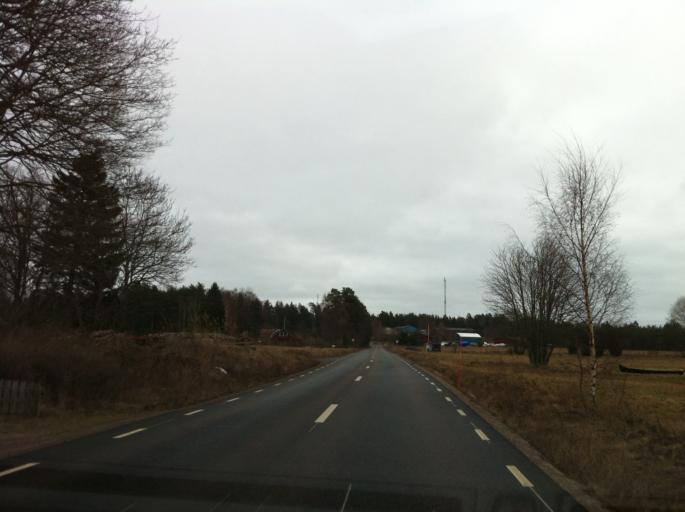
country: SE
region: Kalmar
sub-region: Vasterviks Kommun
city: Overum
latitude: 57.9069
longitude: 16.2326
